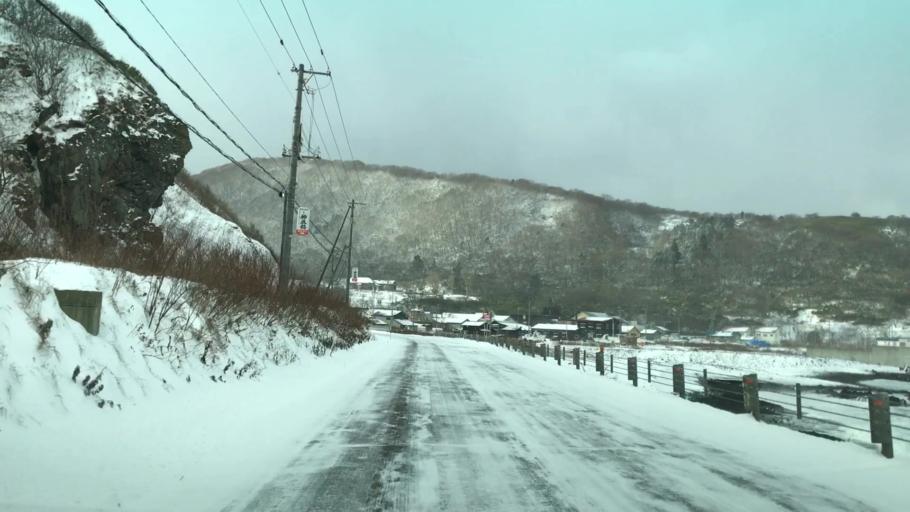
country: JP
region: Hokkaido
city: Iwanai
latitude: 43.3296
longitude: 140.3829
